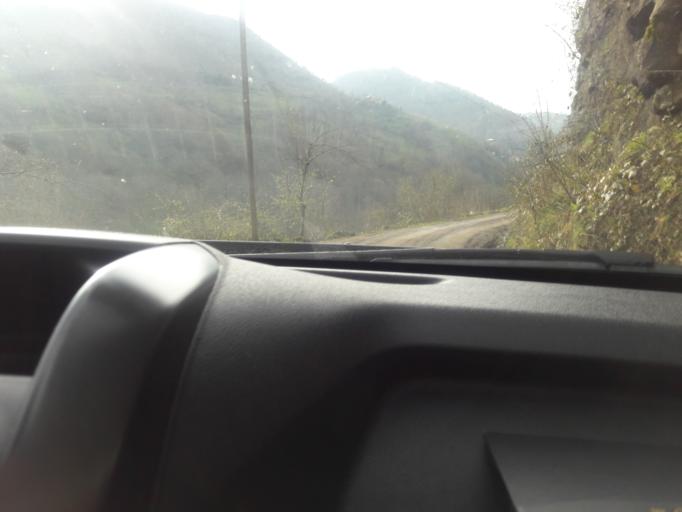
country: TR
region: Trabzon
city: Salpazari
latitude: 40.9677
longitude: 39.1956
